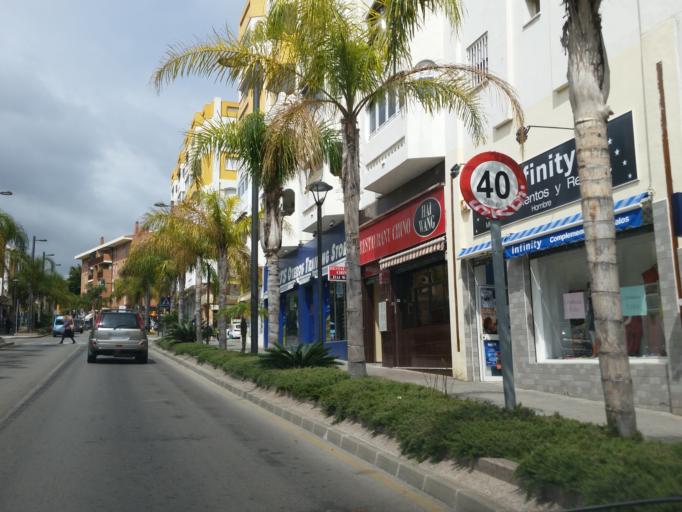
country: ES
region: Andalusia
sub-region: Provincia de Malaga
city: Benalmadena
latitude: 36.5974
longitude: -4.5313
